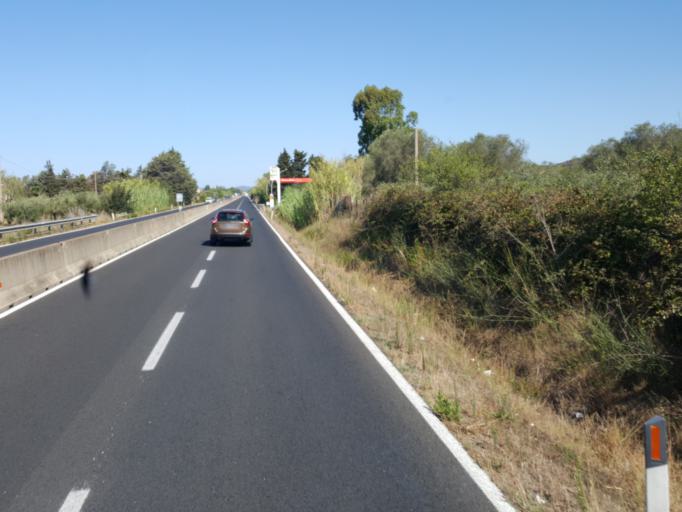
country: IT
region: Tuscany
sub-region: Provincia di Grosseto
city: Orbetello Scalo
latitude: 42.4581
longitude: 11.2481
